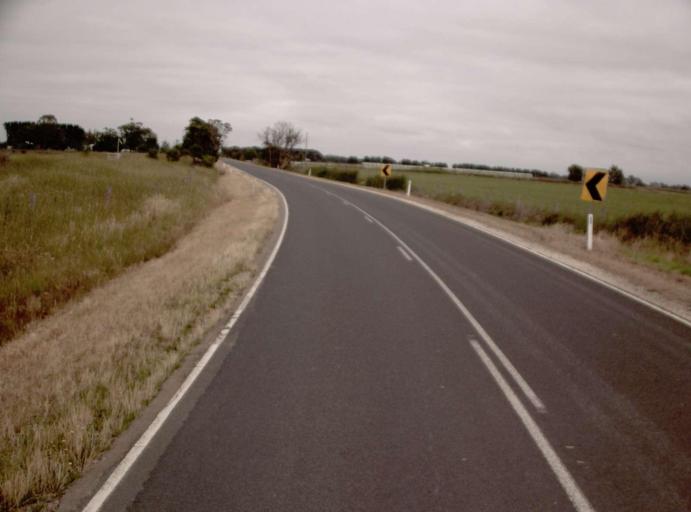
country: AU
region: Victoria
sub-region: Wellington
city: Sale
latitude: -38.0573
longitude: 146.9668
